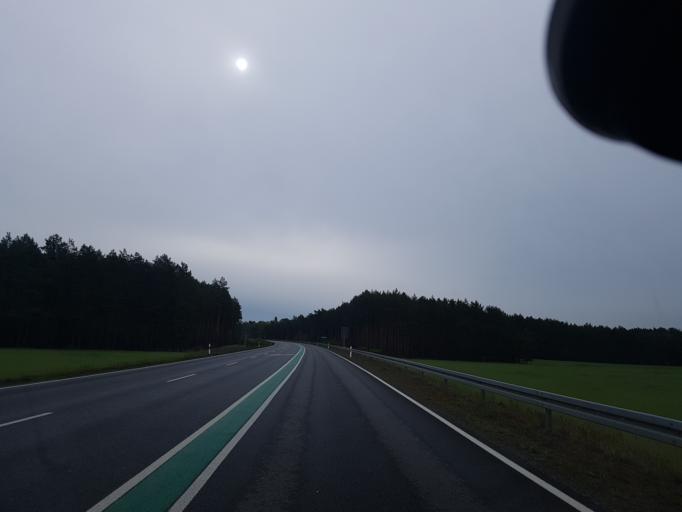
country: DE
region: Brandenburg
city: Drebkau
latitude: 51.6376
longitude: 14.2134
